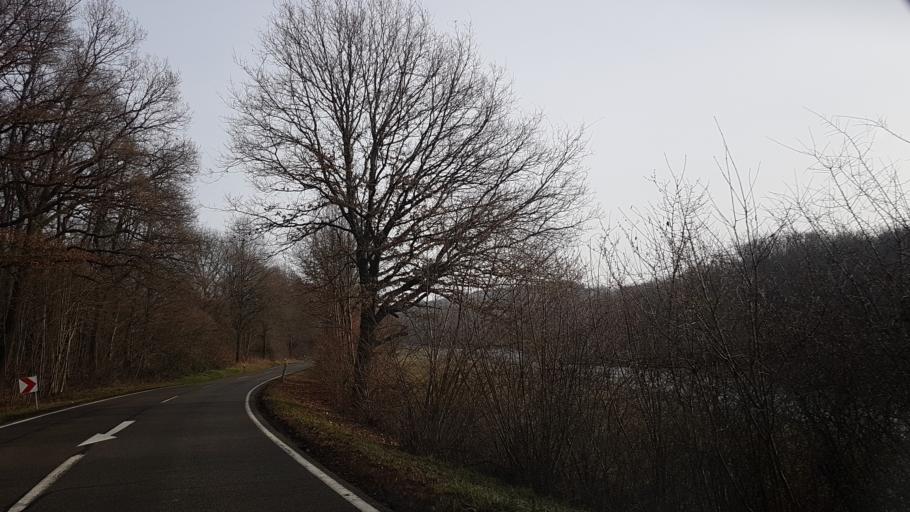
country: DE
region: Saarland
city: Sankt Wendel
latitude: 49.4882
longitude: 7.1888
